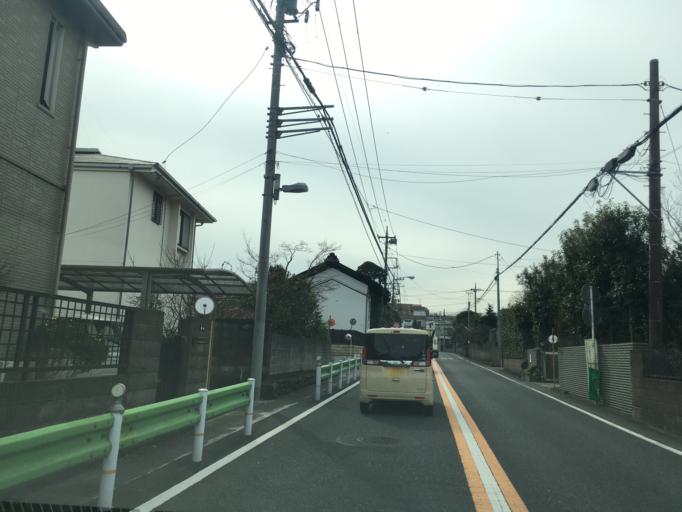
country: JP
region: Tokyo
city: Hino
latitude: 35.6458
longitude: 139.4383
